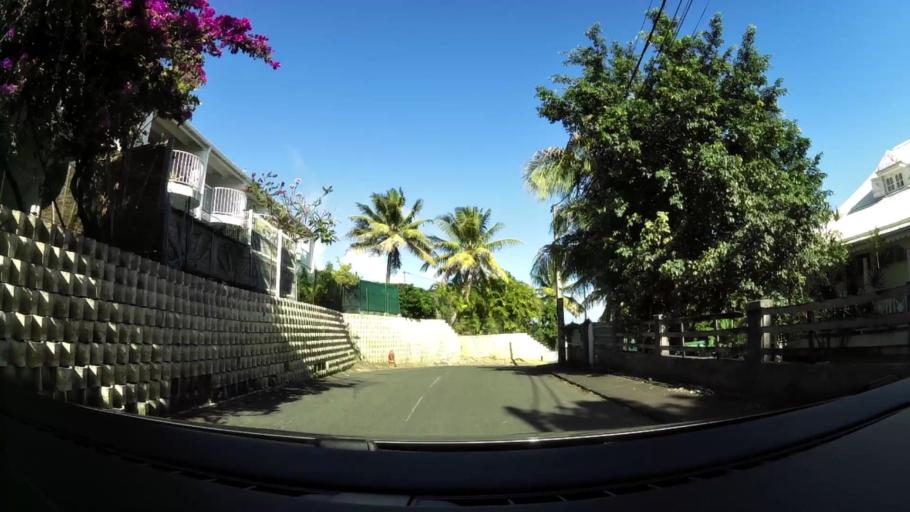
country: GP
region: Guadeloupe
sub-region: Guadeloupe
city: Le Gosier
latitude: 16.2036
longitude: -61.4751
